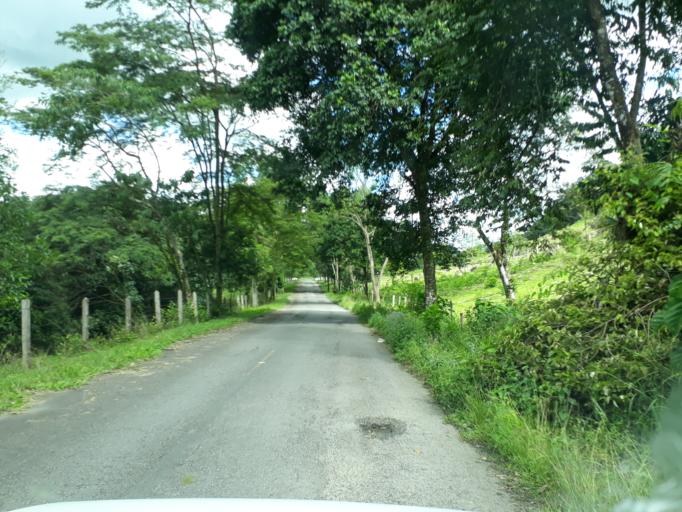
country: CO
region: Cundinamarca
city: Medina
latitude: 4.5526
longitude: -73.3607
